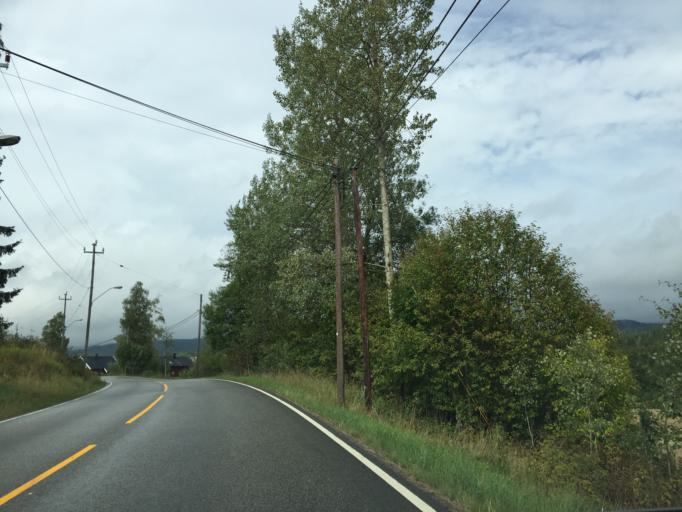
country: NO
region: Akershus
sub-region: Baerum
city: Lysaker
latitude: 60.0176
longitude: 10.5984
